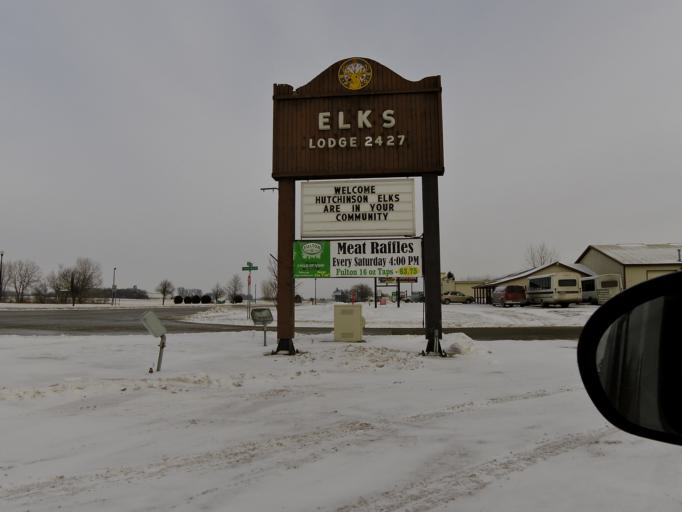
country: US
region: Minnesota
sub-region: McLeod County
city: Hutchinson
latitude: 44.8952
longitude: -94.3484
